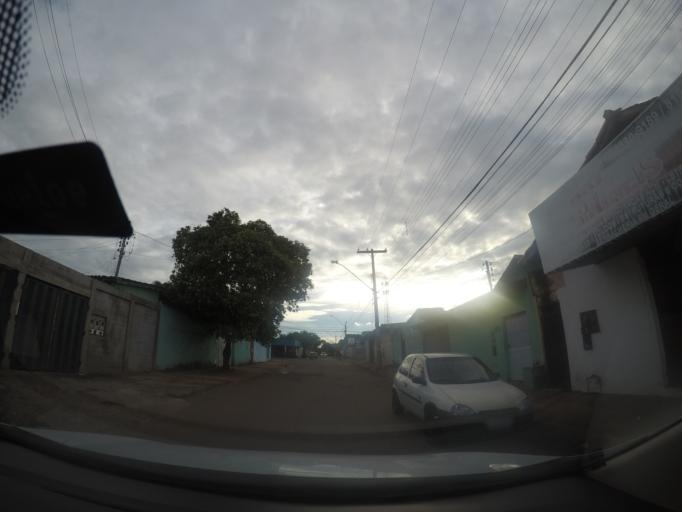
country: BR
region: Goias
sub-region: Goiania
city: Goiania
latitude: -16.6467
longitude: -49.3278
